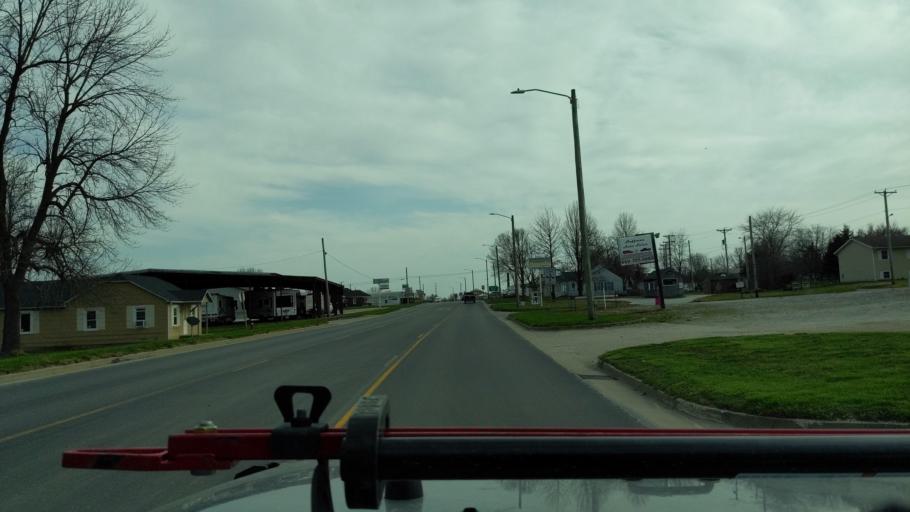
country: US
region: Missouri
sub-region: Macon County
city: Macon
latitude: 39.7283
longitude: -92.4659
